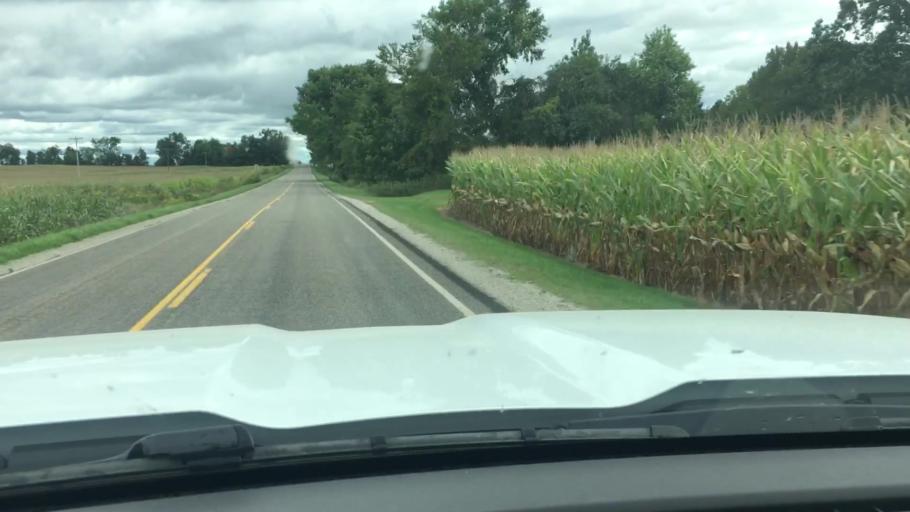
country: US
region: Michigan
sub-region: Montcalm County
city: Carson City
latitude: 43.2421
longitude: -84.7776
